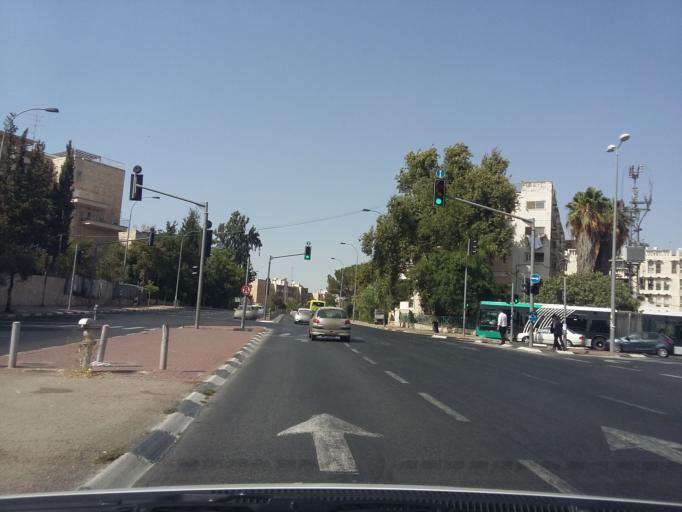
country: IL
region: Jerusalem
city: West Jerusalem
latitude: 31.7968
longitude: 35.2223
